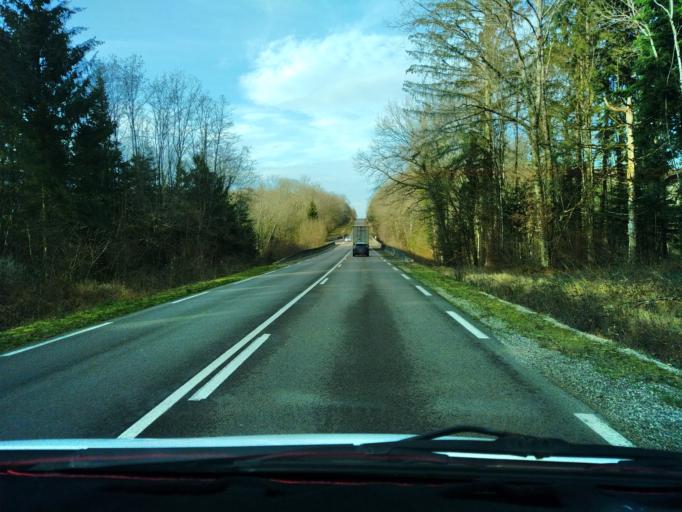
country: FR
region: Franche-Comte
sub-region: Departement de la Haute-Saone
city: Gray
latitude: 47.4041
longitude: 5.6394
